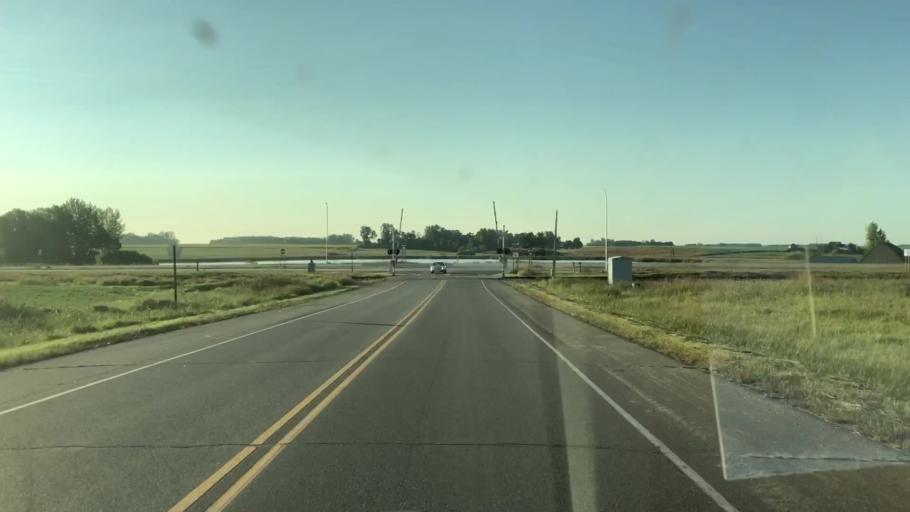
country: US
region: Minnesota
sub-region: Nobles County
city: Worthington
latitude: 43.5983
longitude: -95.6344
